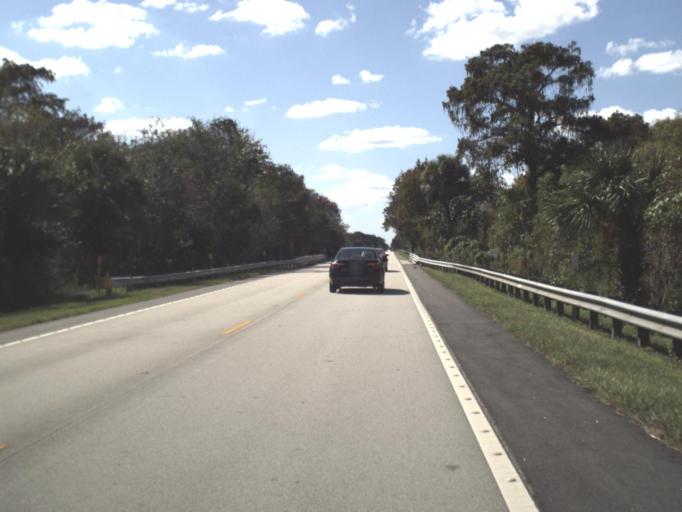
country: US
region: Florida
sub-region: Collier County
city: Lely Resort
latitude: 25.8670
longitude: -81.1332
